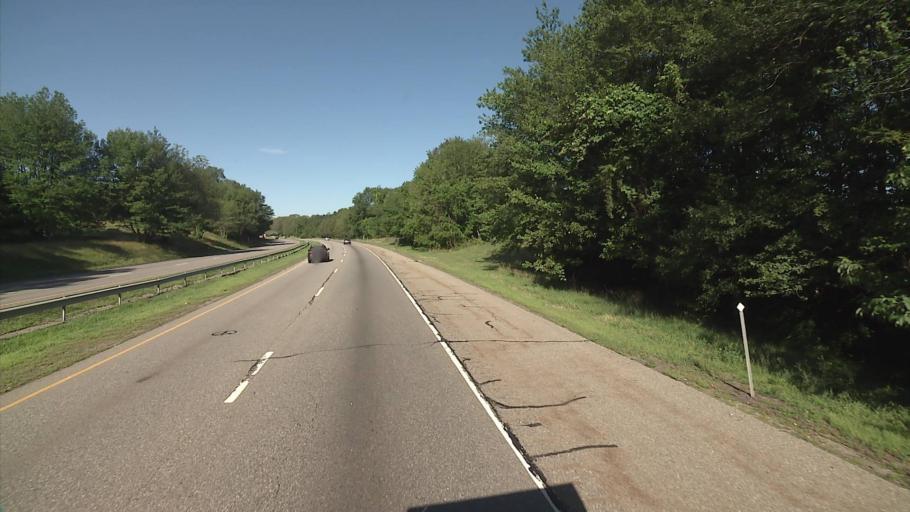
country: US
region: Connecticut
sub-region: New London County
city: Baltic
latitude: 41.5837
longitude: -72.0631
